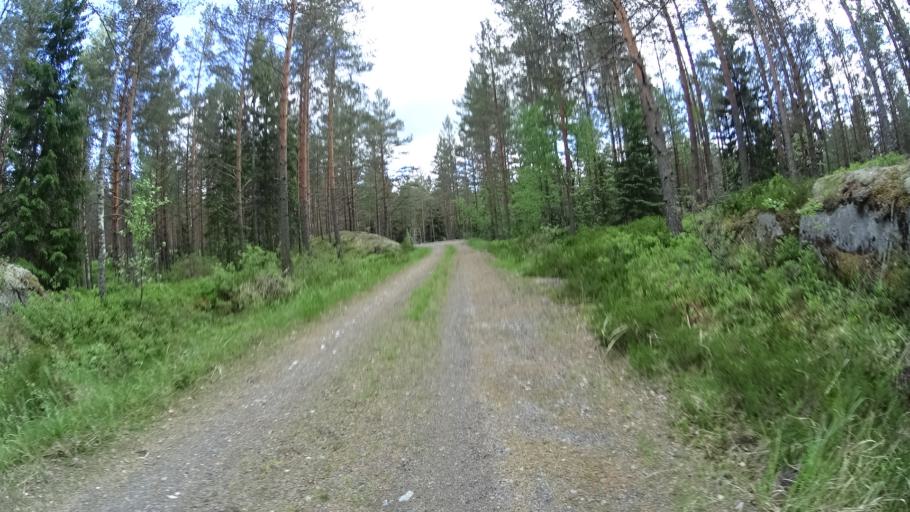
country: FI
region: Varsinais-Suomi
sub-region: Salo
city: Kisko
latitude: 60.1833
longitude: 23.5536
